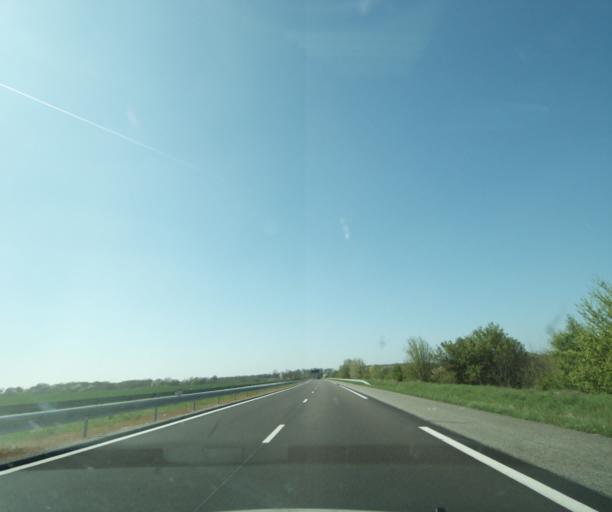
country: FR
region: Centre
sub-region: Departement du Loiret
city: Briare
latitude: 47.6346
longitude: 2.7792
